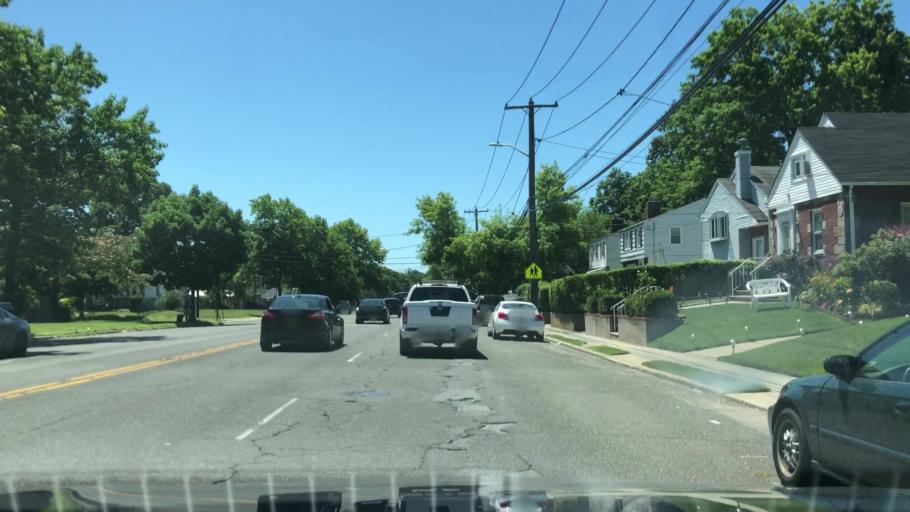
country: US
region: New York
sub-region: Nassau County
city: Hempstead
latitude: 40.7019
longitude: -73.6315
